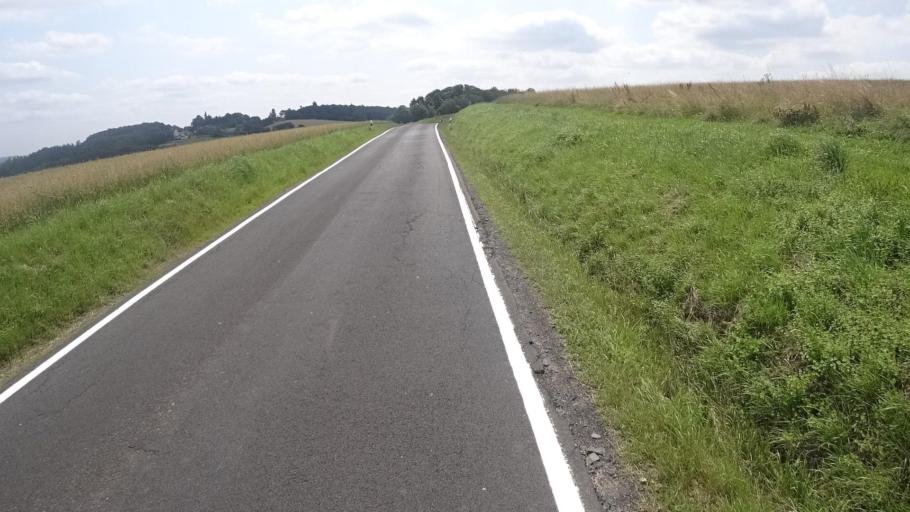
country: DE
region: Rheinland-Pfalz
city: Sankt Katharinen
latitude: 50.5886
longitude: 7.3562
